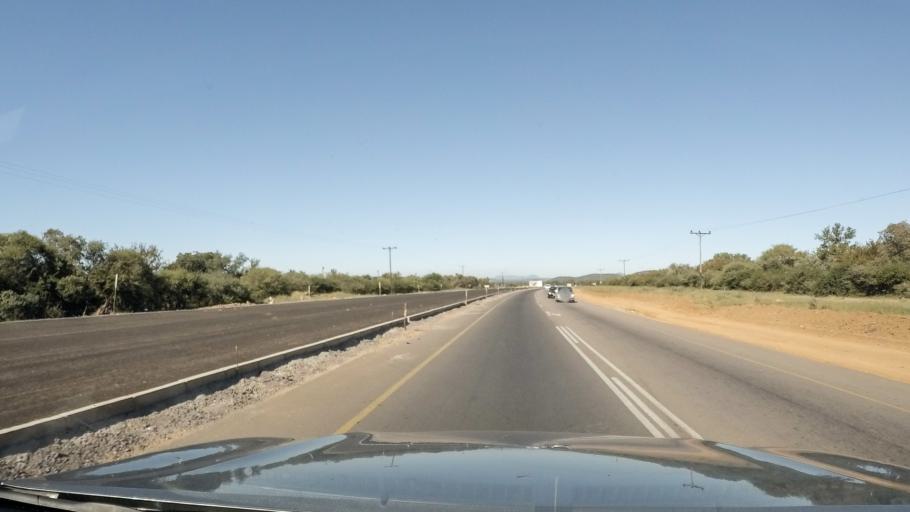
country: BW
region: South East
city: Gaborone
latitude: -24.7130
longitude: 25.8653
